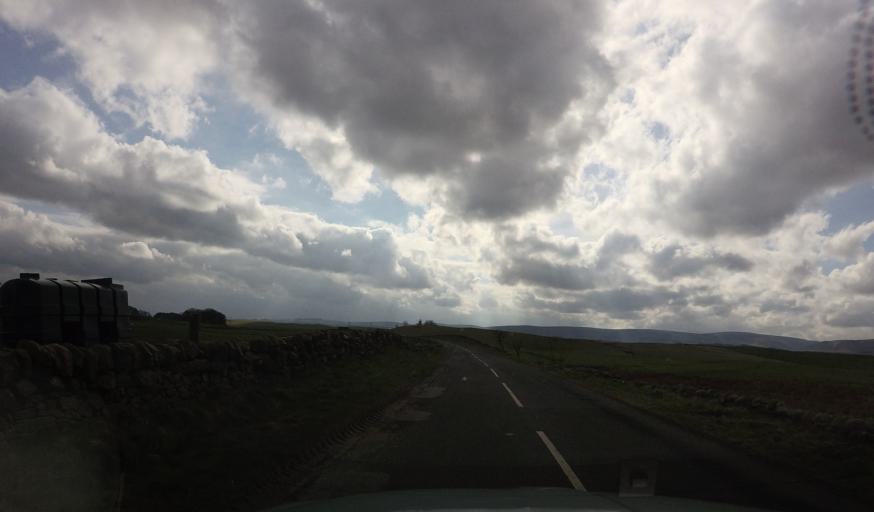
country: GB
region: Scotland
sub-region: Midlothian
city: Penicuik
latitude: 55.8002
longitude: -3.1612
